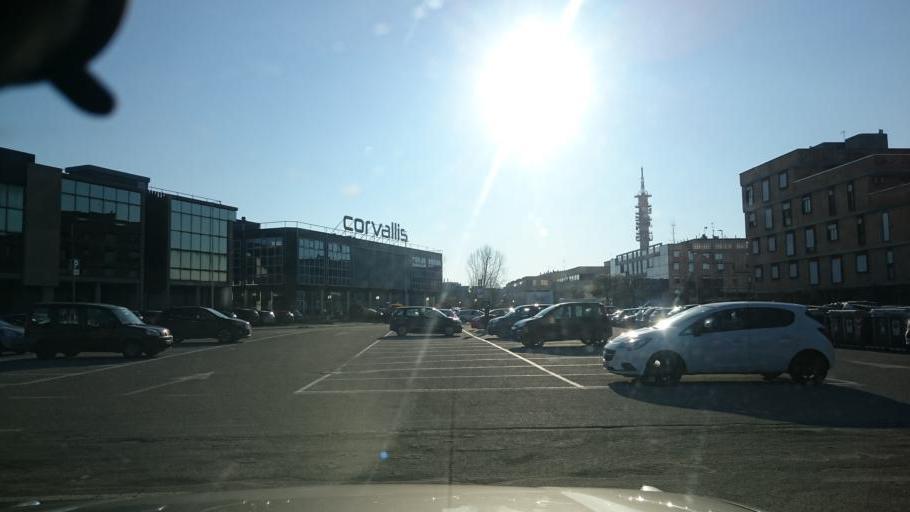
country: IT
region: Veneto
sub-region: Provincia di Padova
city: Padova
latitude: 45.4100
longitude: 11.9141
